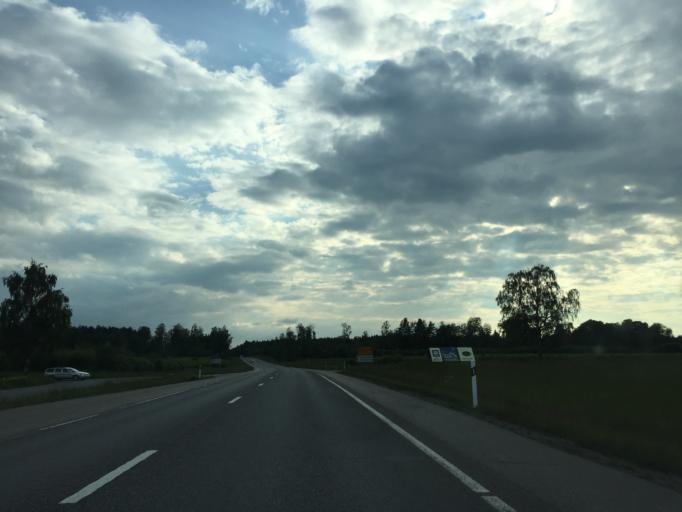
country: SE
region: OErebro
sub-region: Lindesbergs Kommun
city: Fellingsbro
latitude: 59.3436
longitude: 15.5822
